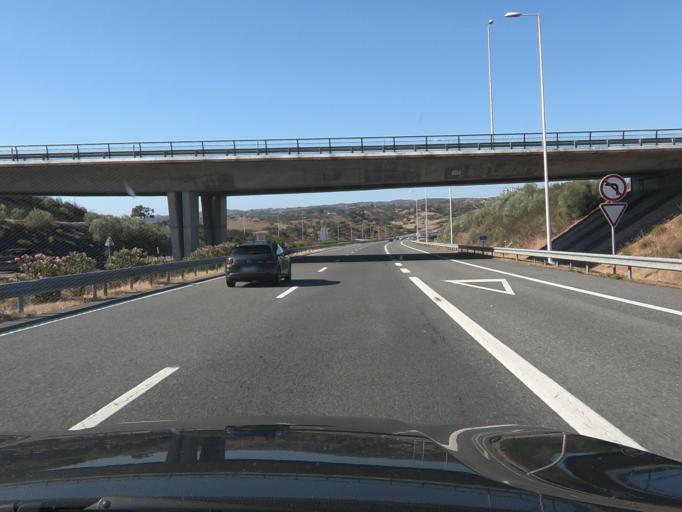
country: PT
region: Beja
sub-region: Almodovar
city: Almodovar
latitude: 37.5218
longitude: -8.1820
